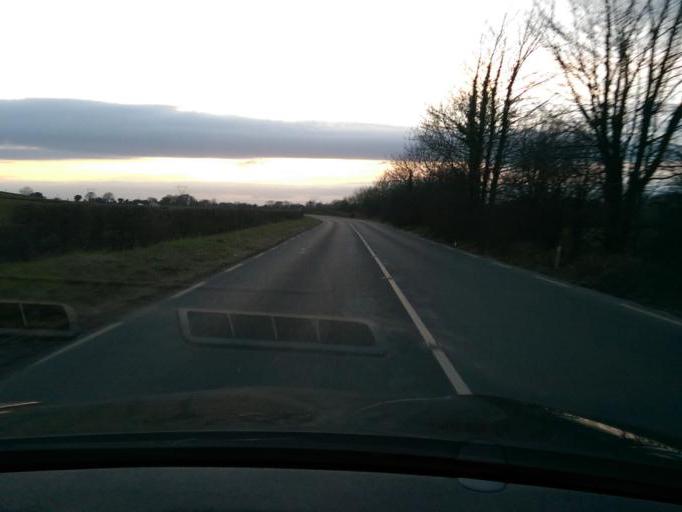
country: IE
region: Leinster
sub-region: Uibh Fhaili
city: Banagher
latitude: 53.1066
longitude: -8.0357
